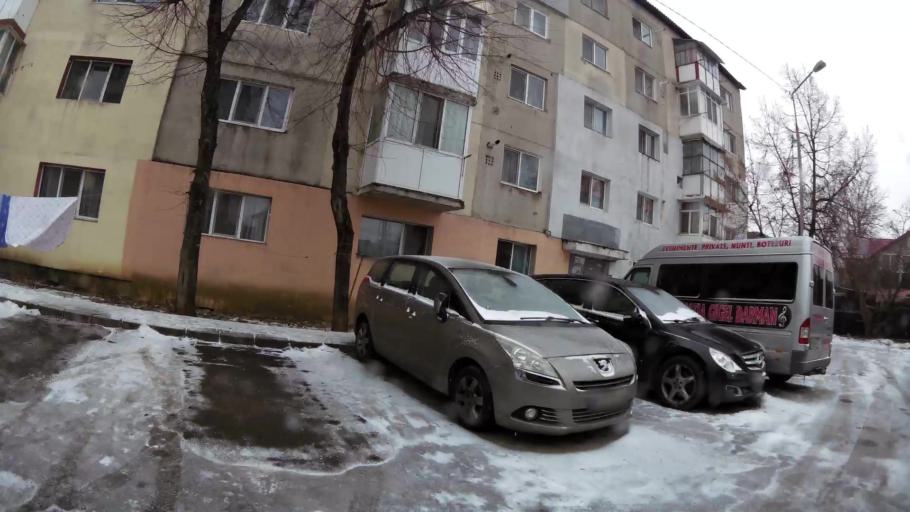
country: RO
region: Dambovita
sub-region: Municipiul Targoviste
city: Targoviste
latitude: 44.9329
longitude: 25.4499
